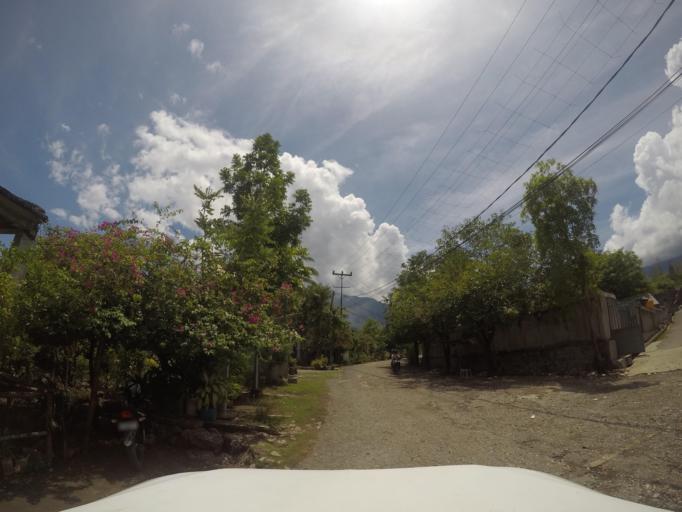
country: TL
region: Bobonaro
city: Maliana
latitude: -8.9953
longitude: 125.2240
